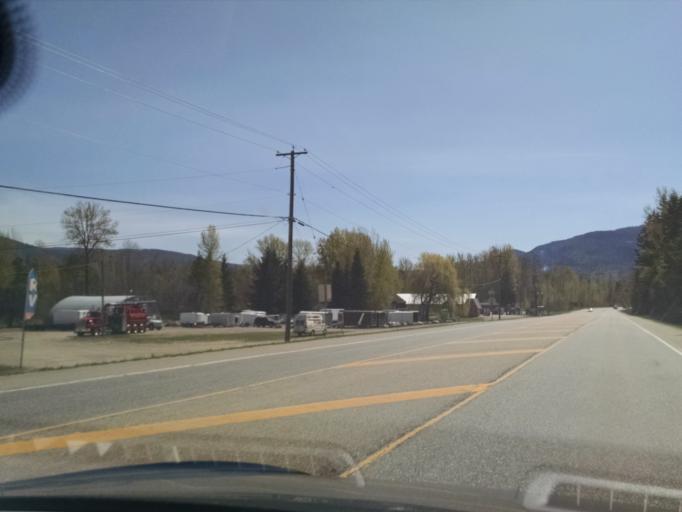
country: CA
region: British Columbia
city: Salmon Arm
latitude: 50.7351
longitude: -119.3187
